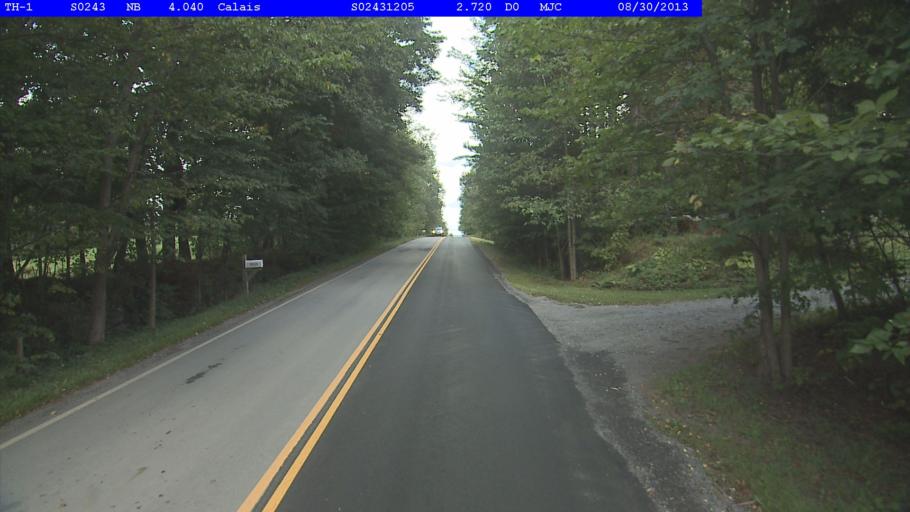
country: US
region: Vermont
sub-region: Washington County
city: Montpelier
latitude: 44.3697
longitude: -72.4992
